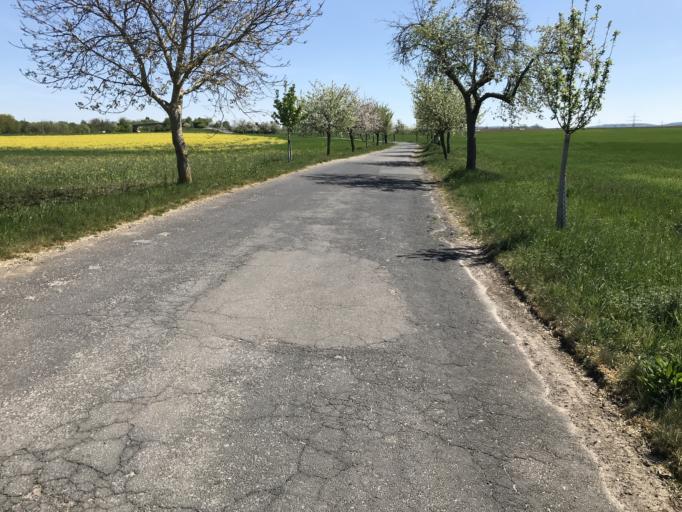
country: DE
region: Bavaria
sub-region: Regierungsbezirk Unterfranken
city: Markt Einersheim
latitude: 49.6874
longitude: 10.2736
